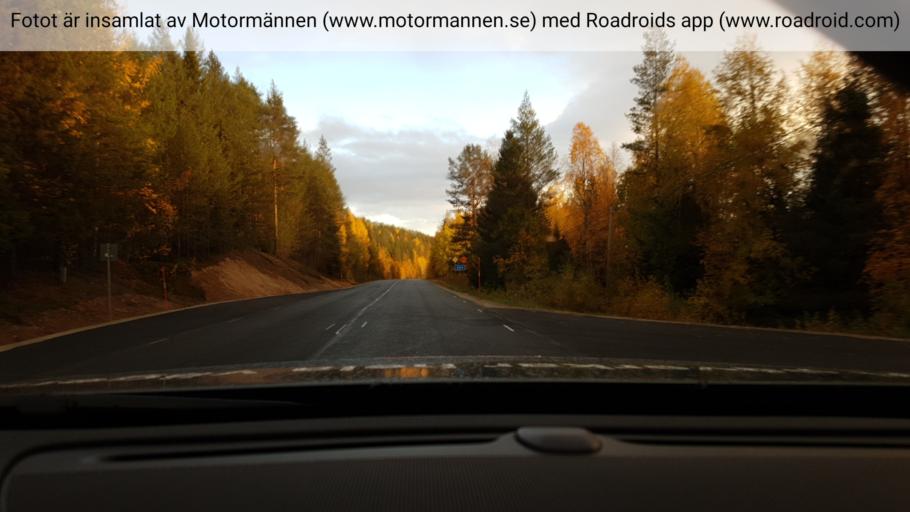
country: SE
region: Norrbotten
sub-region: Overkalix Kommun
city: OEverkalix
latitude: 66.4887
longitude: 22.7786
